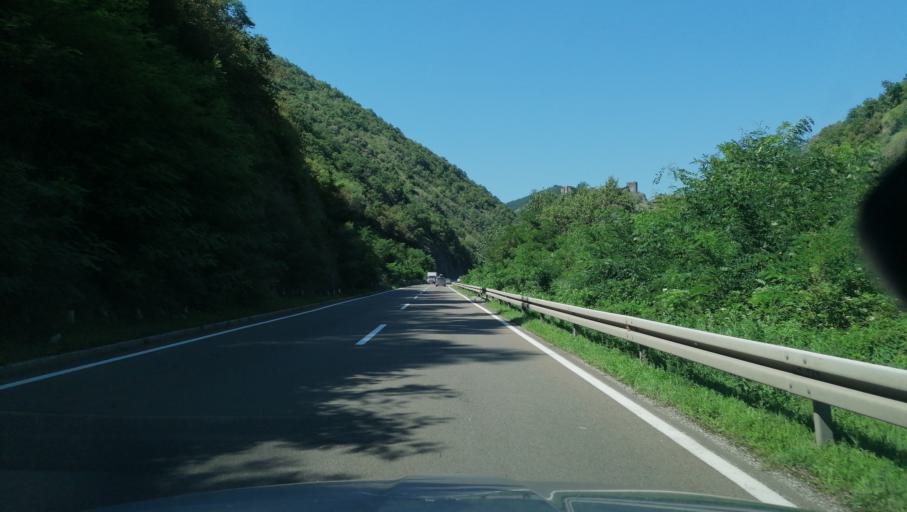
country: RS
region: Central Serbia
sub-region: Raski Okrug
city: Kraljevo
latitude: 43.6053
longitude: 20.5559
